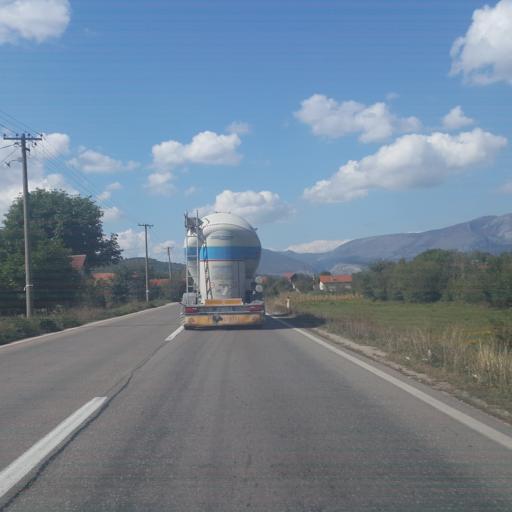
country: RS
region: Central Serbia
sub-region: Pirotski Okrug
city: Bela Palanka
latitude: 43.2677
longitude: 22.2456
